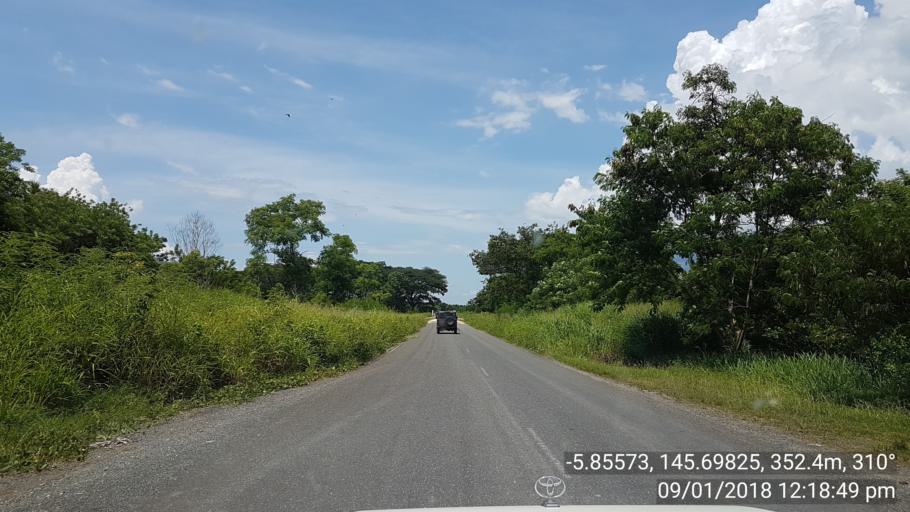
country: PG
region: Eastern Highlands
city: Goroka
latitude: -5.8558
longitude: 145.6983
